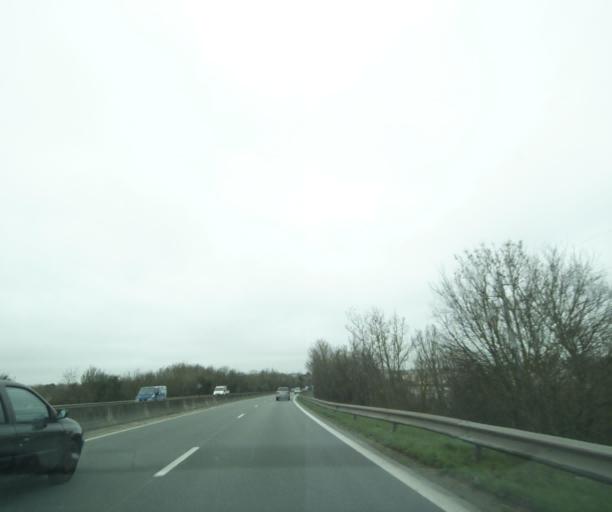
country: FR
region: Poitou-Charentes
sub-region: Departement de la Charente-Maritime
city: Puilboreau
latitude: 46.1632
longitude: -1.1220
